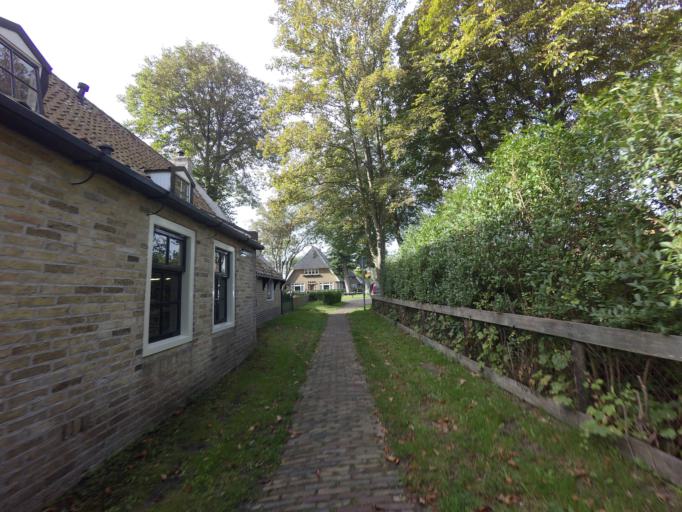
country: NL
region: Friesland
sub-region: Gemeente Ameland
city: Nes
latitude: 53.4447
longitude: 5.7741
